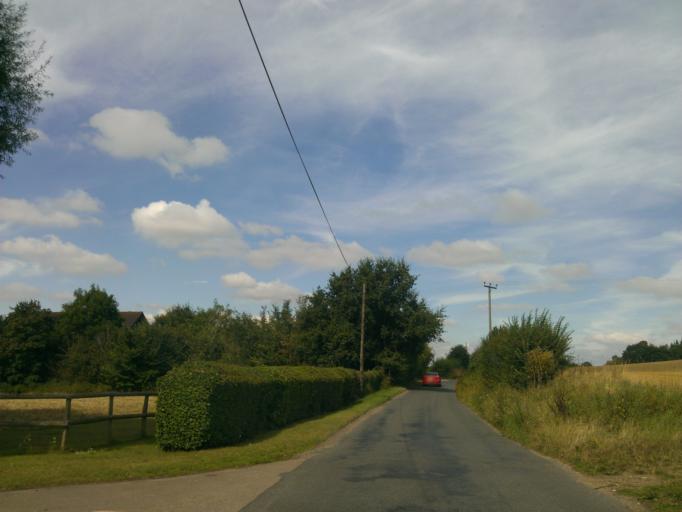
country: GB
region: England
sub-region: Essex
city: Sible Hedingham
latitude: 51.9822
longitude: 0.6016
